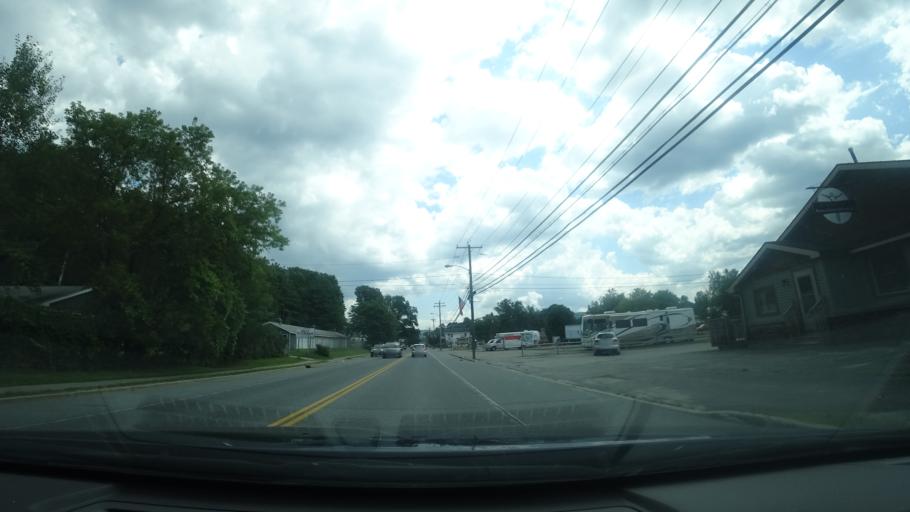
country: US
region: New York
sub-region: Warren County
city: Warrensburg
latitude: 43.5015
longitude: -73.7830
